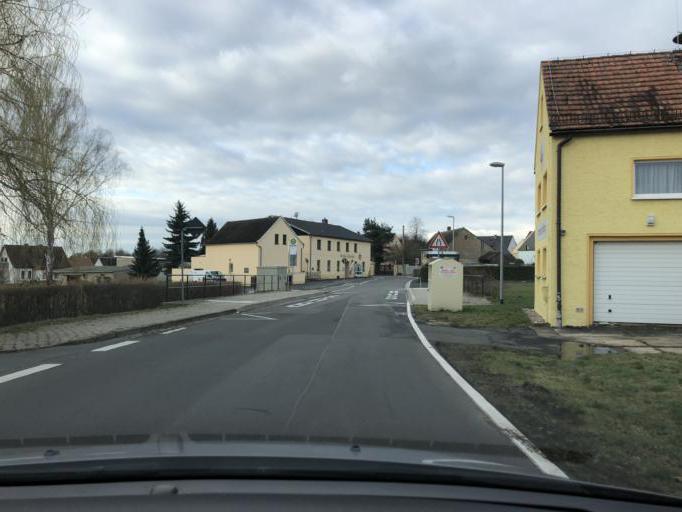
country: DE
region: Saxony
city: Grossbothen
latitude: 51.1912
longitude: 12.7869
